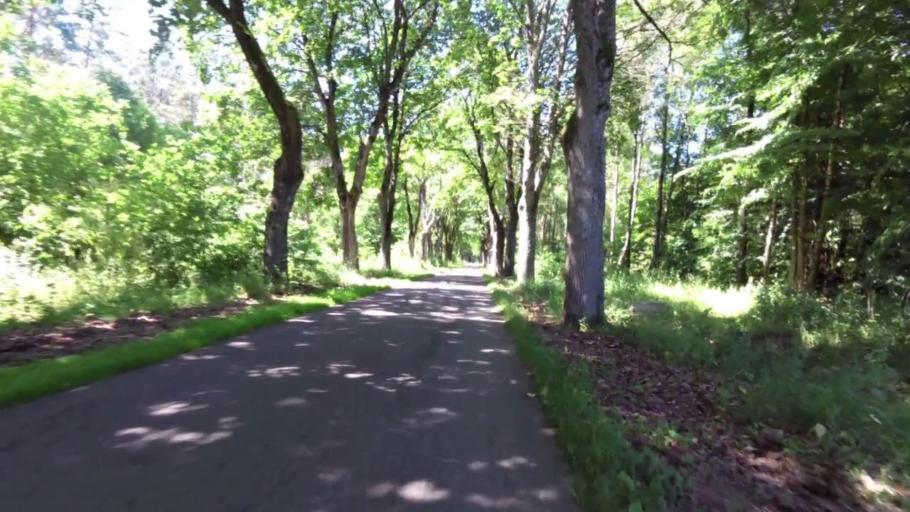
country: PL
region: West Pomeranian Voivodeship
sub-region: Powiat swidwinski
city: Rabino
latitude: 53.8593
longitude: 15.9879
